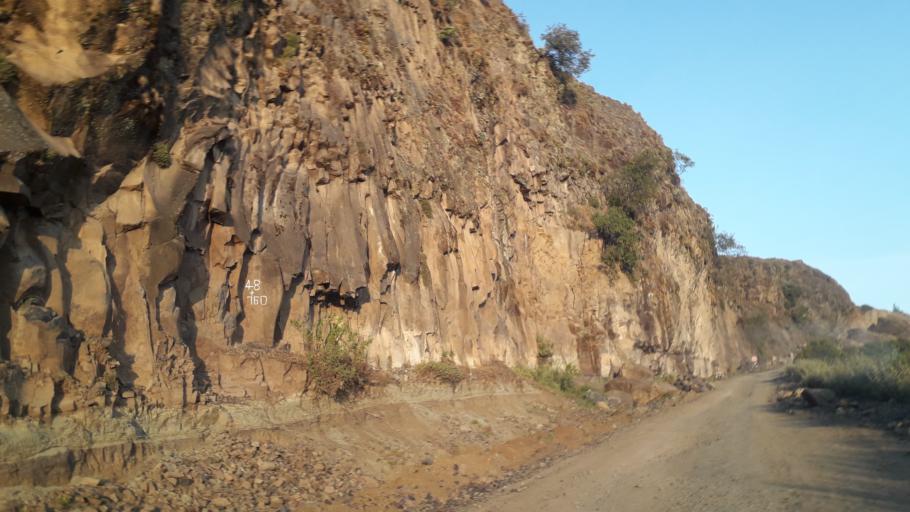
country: ET
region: Amhara
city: Lalibela
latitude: 11.5538
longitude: 39.2191
